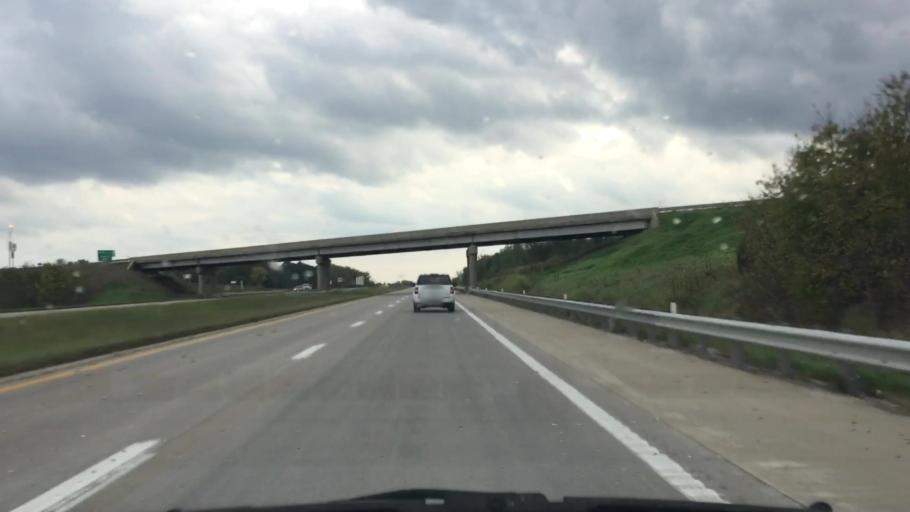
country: US
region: Missouri
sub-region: Clinton County
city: Cameron
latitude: 39.6689
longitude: -94.2356
